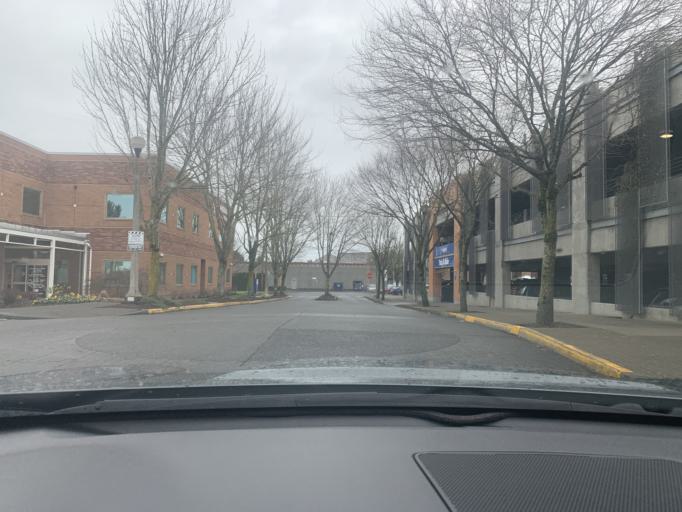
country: US
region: Oregon
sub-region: Multnomah County
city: Lents
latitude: 45.5321
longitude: -122.5634
